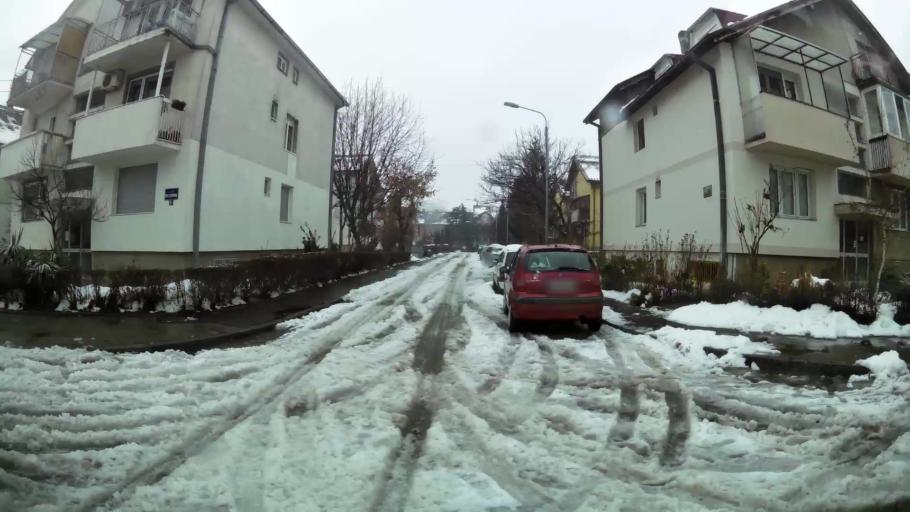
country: RS
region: Central Serbia
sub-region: Belgrade
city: Zemun
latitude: 44.8743
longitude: 20.3231
